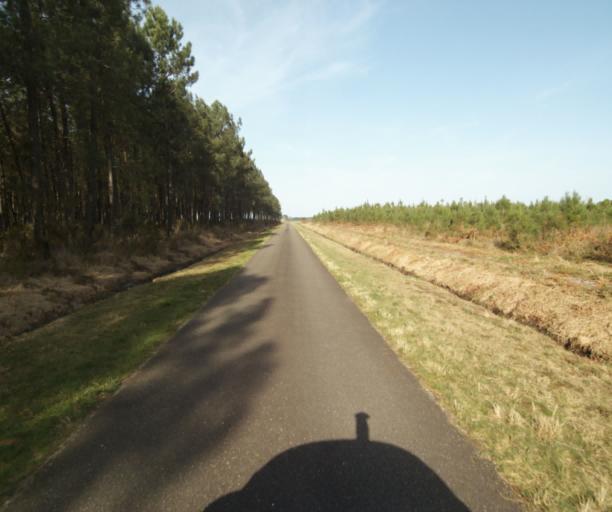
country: FR
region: Aquitaine
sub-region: Departement des Landes
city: Sarbazan
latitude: 44.1365
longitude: -0.1569
